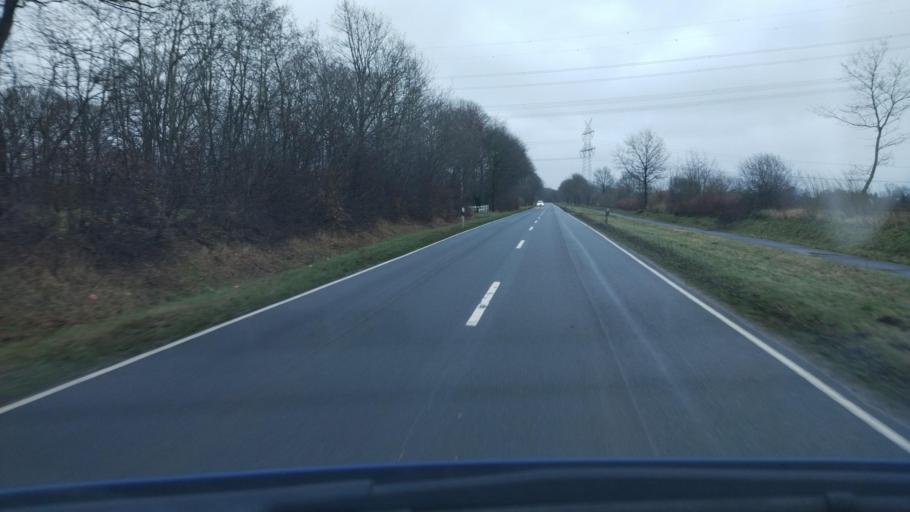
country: DE
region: Schleswig-Holstein
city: Gross Rheide
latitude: 54.4461
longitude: 9.4180
